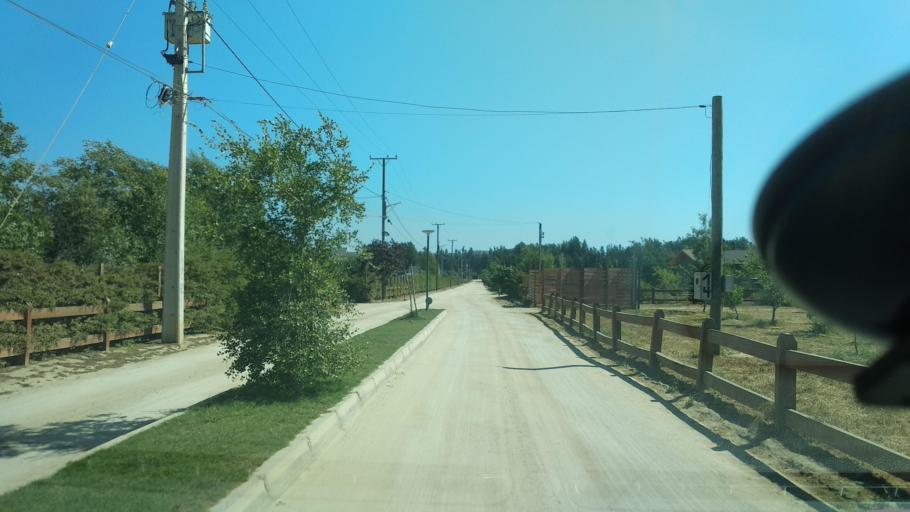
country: CL
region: Valparaiso
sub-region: Provincia de Marga Marga
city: Limache
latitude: -32.9707
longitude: -71.3081
